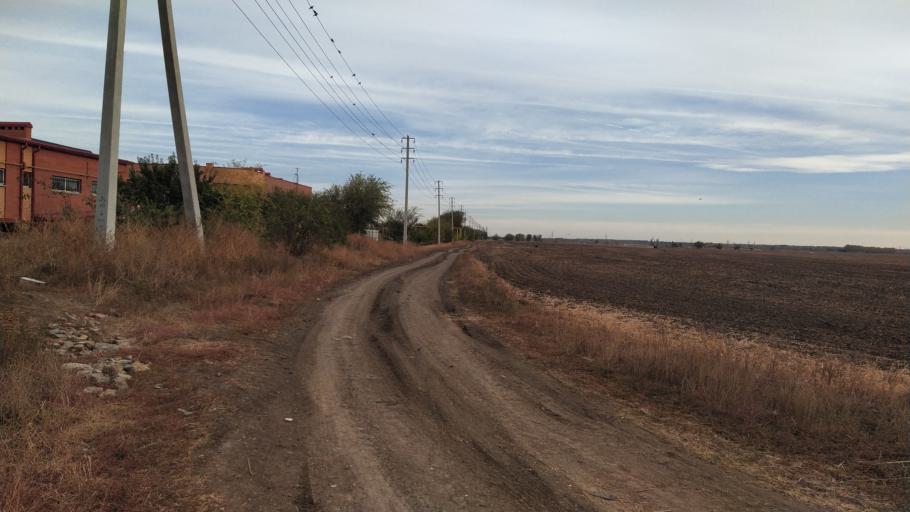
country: RU
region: Rostov
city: Bataysk
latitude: 47.1129
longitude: 39.6786
